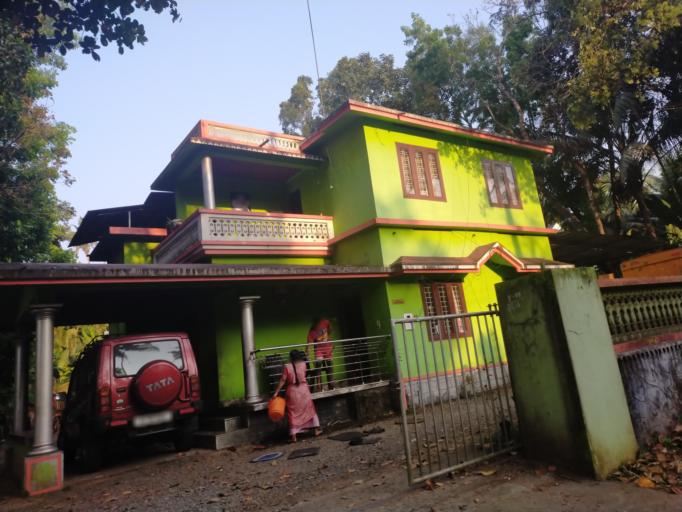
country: IN
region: Kerala
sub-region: Kottayam
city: Vaikam
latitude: 9.7523
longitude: 76.5043
